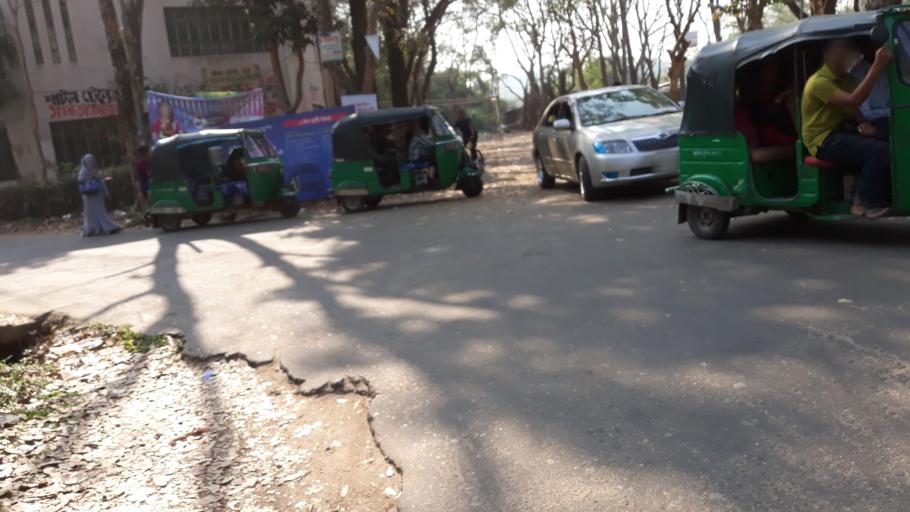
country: BD
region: Chittagong
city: Chittagong
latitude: 22.4711
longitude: 91.7839
